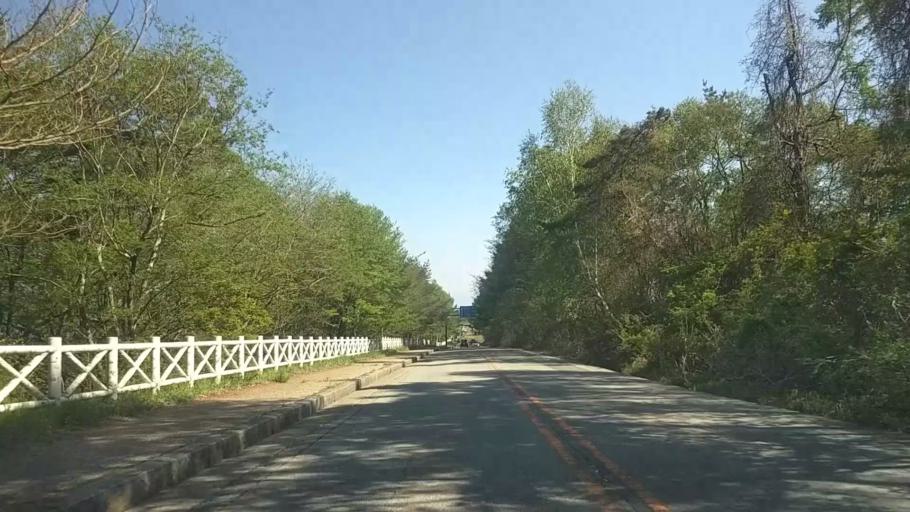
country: JP
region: Yamanashi
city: Nirasaki
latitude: 35.9266
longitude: 138.4072
